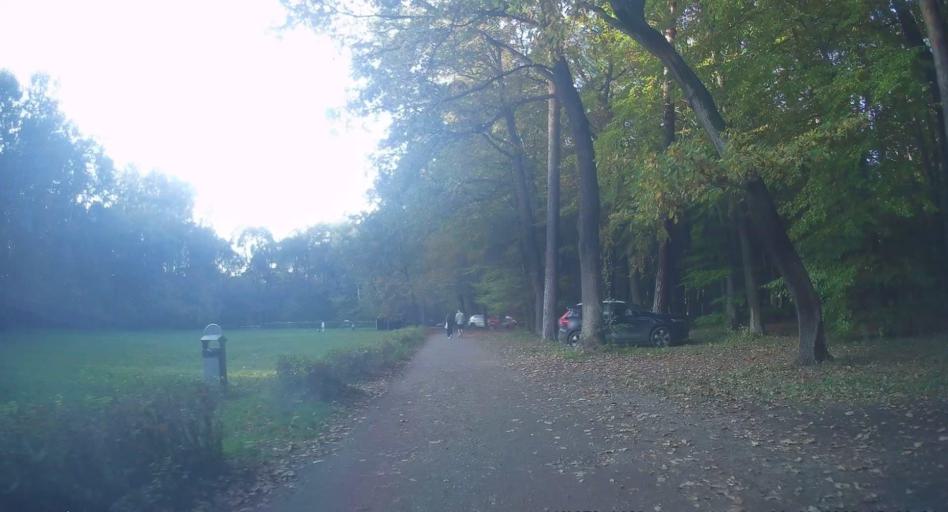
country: PL
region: Lesser Poland Voivodeship
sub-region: Powiat wielicki
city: Niepolomice
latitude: 50.0138
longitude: 20.2410
